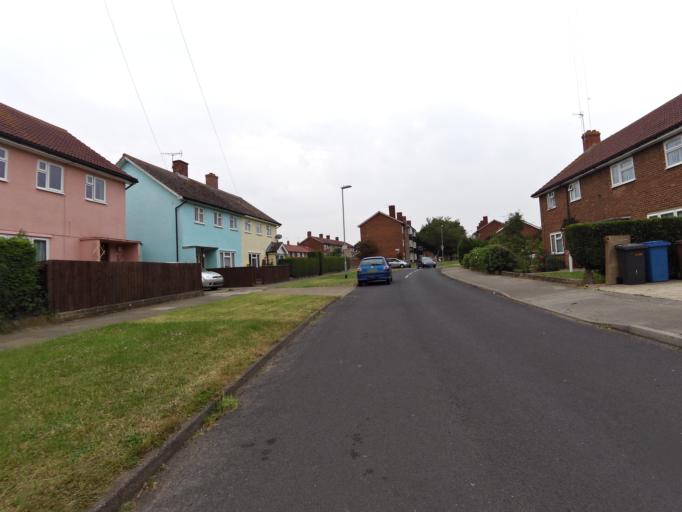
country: GB
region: England
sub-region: Suffolk
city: Ipswich
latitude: 52.0840
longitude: 1.1353
